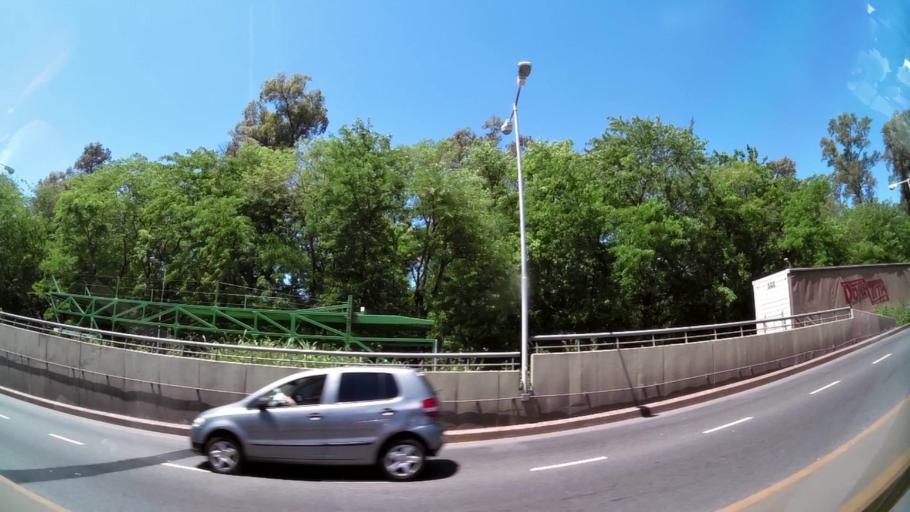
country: AR
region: Buenos Aires
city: Hurlingham
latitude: -34.5034
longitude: -58.6493
